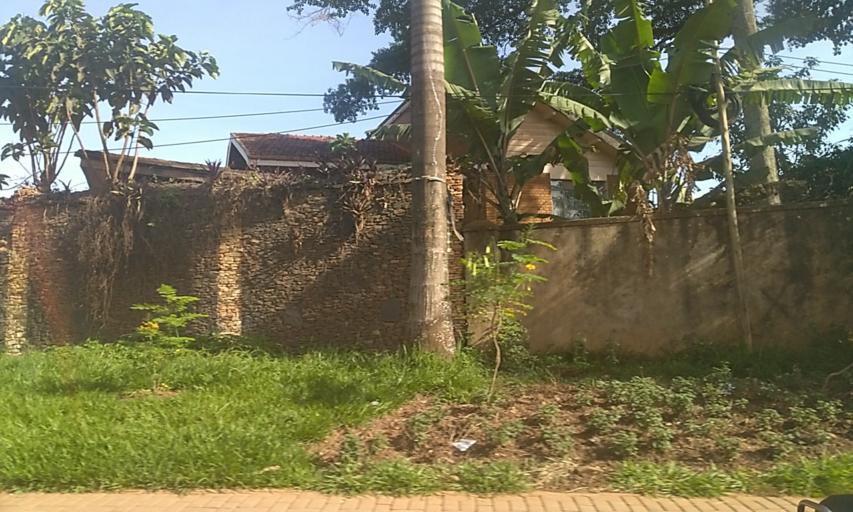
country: UG
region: Central Region
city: Kampala Central Division
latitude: 0.3480
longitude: 32.5983
